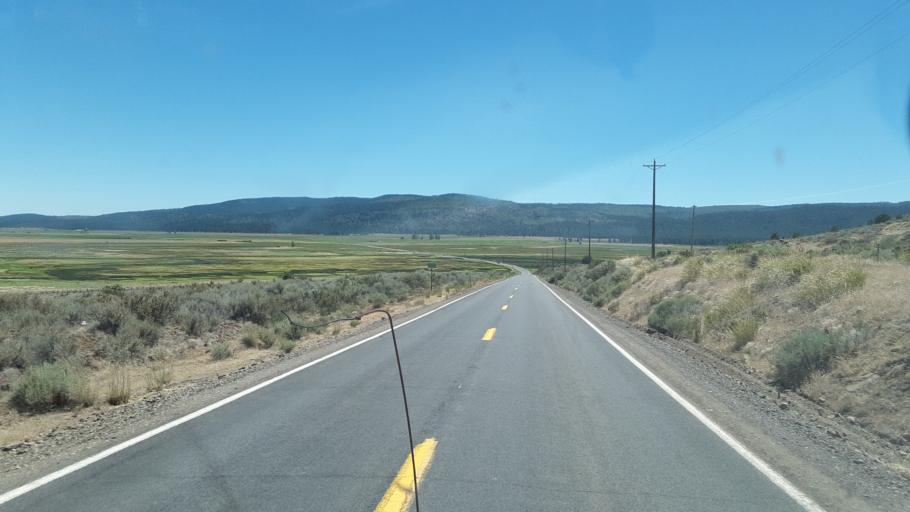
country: US
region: California
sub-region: Lassen County
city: Susanville
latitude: 40.5743
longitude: -120.6420
